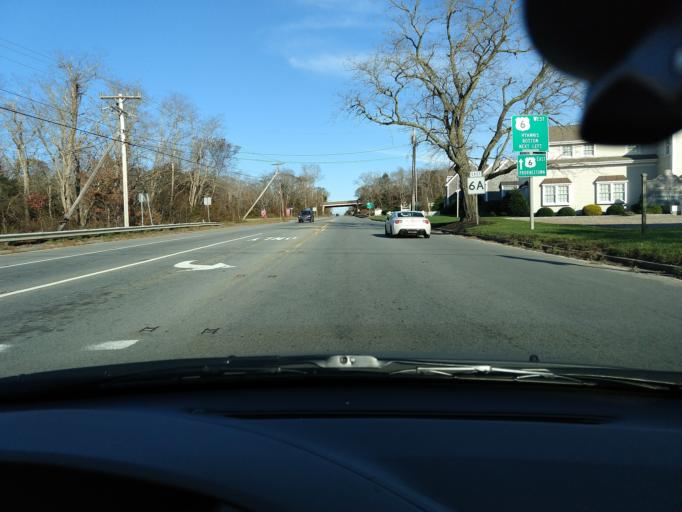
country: US
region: Massachusetts
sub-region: Barnstable County
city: Orleans
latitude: 41.7767
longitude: -70.0060
